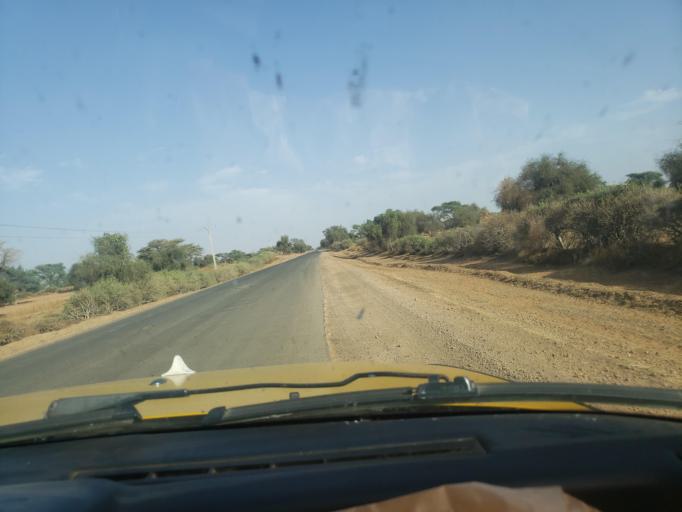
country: SN
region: Louga
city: Louga
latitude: 15.5090
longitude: -15.9768
